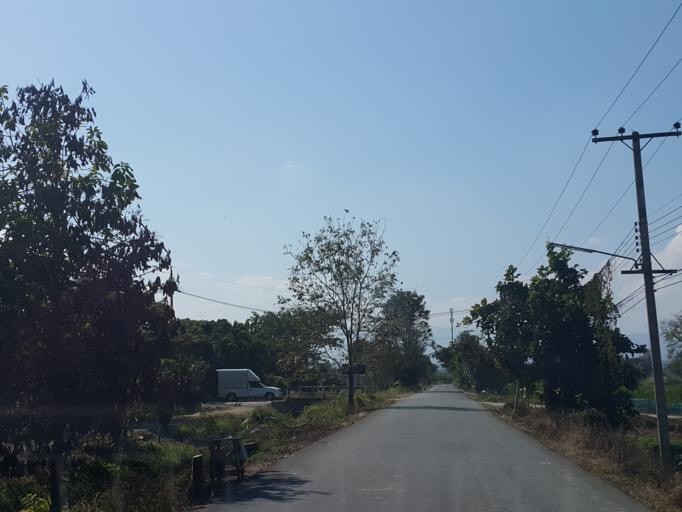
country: TH
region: Chiang Mai
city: Mae Taeng
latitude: 19.0379
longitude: 98.9743
